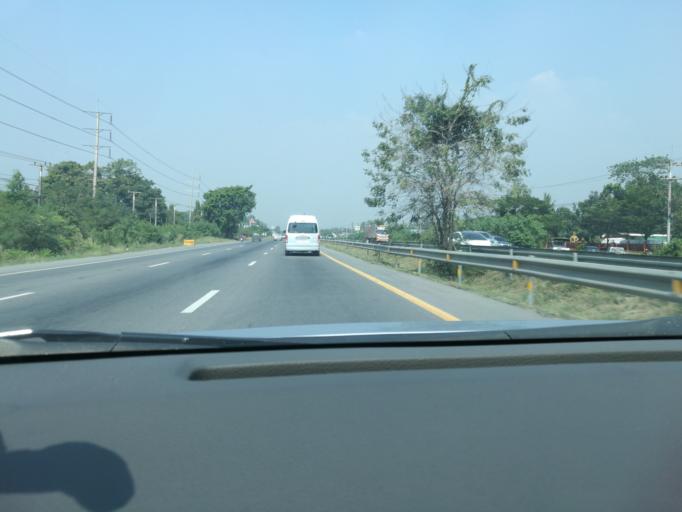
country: TH
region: Sara Buri
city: Chaloem Phra Kiat
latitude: 14.6240
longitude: 100.8906
